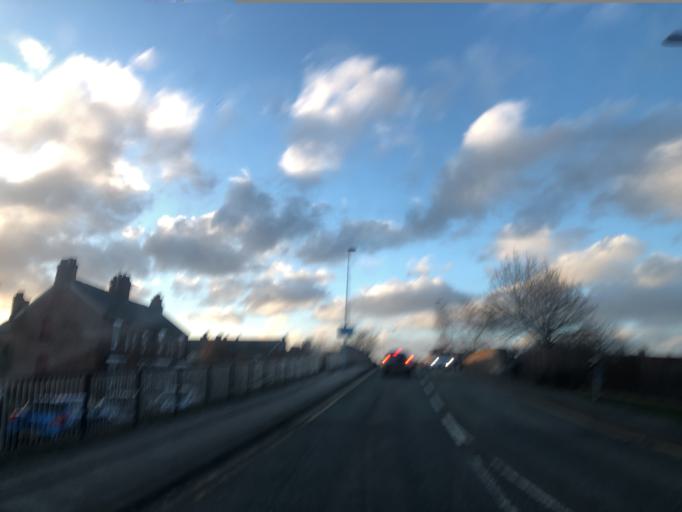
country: GB
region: England
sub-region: Cheshire West and Chester
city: Marston
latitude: 53.2607
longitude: -2.4965
